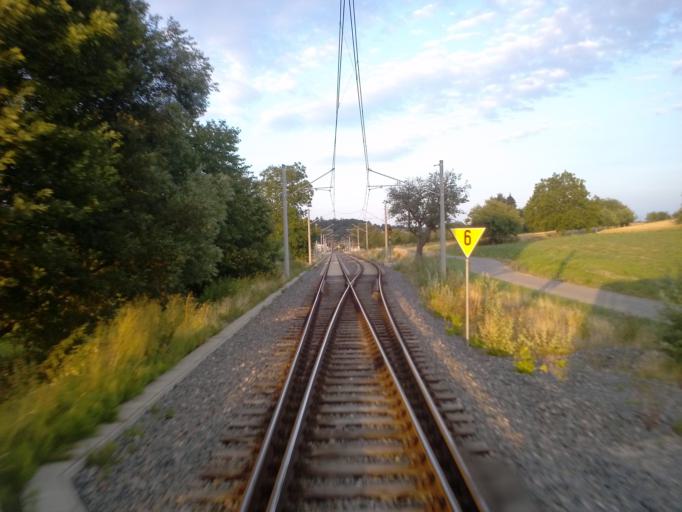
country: DE
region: Baden-Wuerttemberg
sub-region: Karlsruhe Region
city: Ettlingen
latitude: 48.9203
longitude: 8.4948
